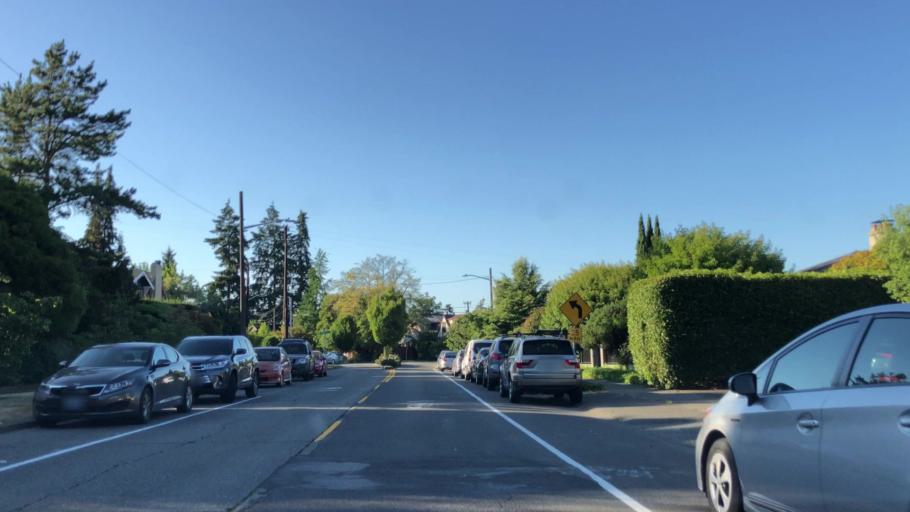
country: US
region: Washington
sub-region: King County
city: Seattle
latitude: 47.6460
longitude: -122.3171
